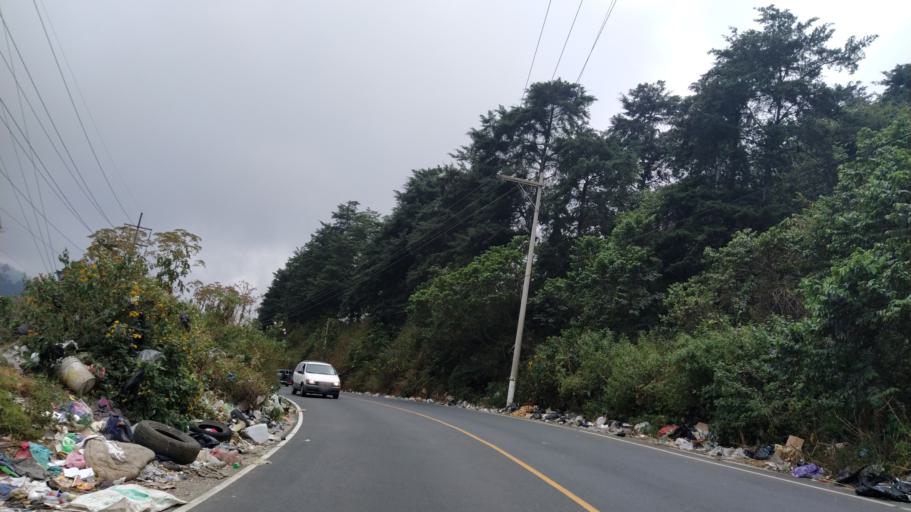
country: GT
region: Quetzaltenango
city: Zunil
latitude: 14.7443
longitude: -91.5151
